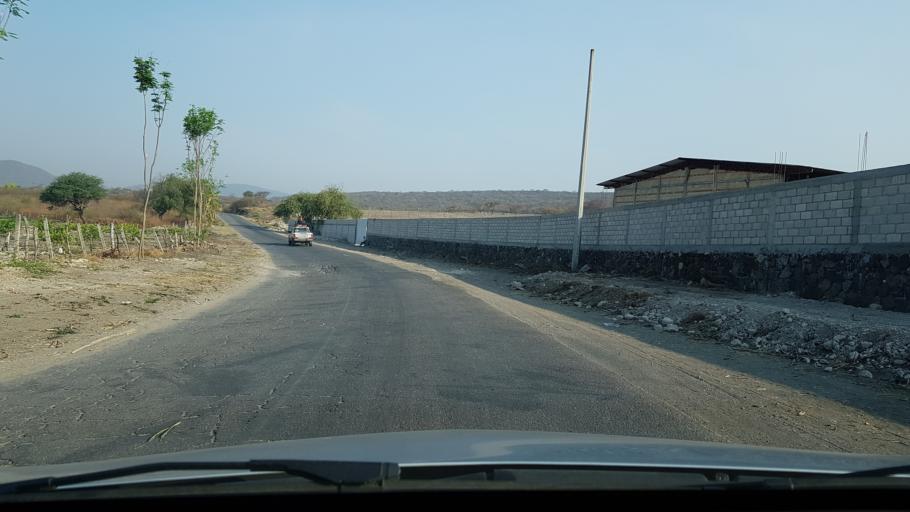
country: MX
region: Morelos
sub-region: Tlaltizapan de Zapata
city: Colonia Palo Prieto (Chipitongo)
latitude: 18.6876
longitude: -99.0928
